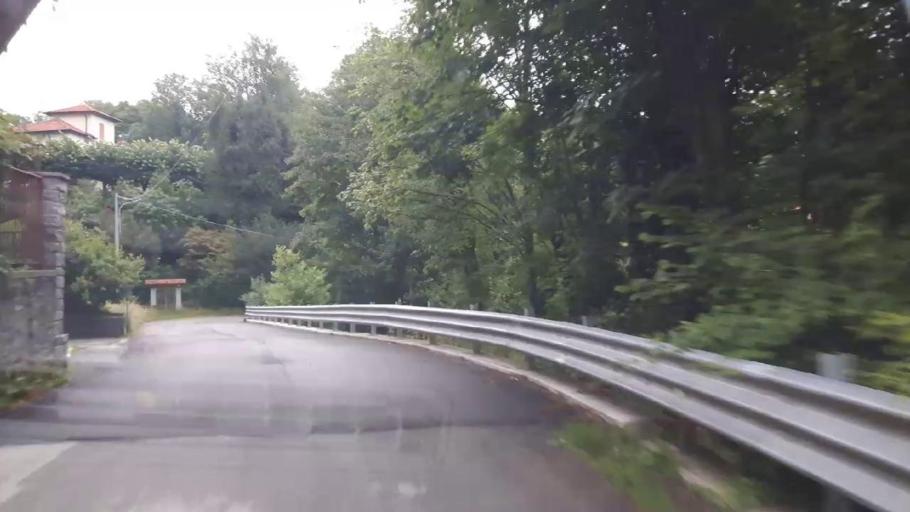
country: IT
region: Piedmont
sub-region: Provincia Verbano-Cusio-Ossola
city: Gignese
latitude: 45.8634
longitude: 8.5077
